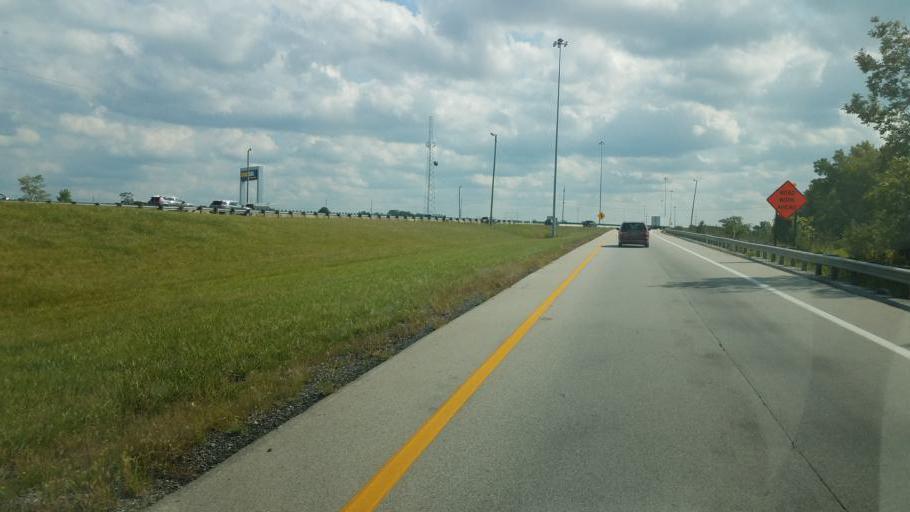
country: US
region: Ohio
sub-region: Cuyahoga County
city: North Randall
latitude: 41.4275
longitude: -81.5084
